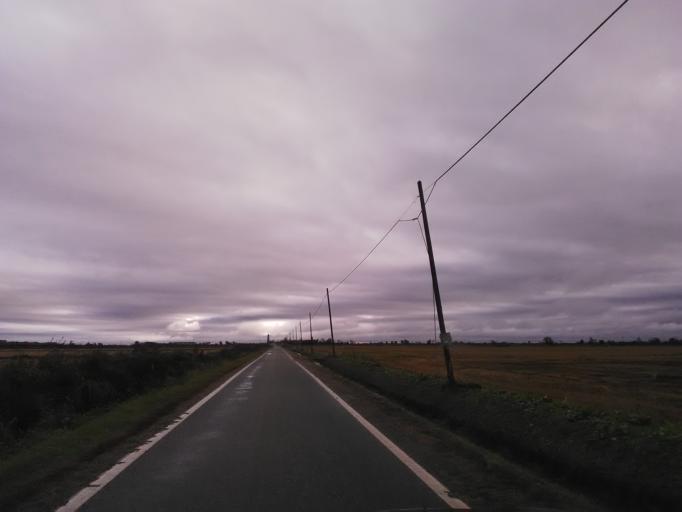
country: IT
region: Piedmont
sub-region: Provincia di Vercelli
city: Carisio
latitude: 45.4029
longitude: 8.2204
